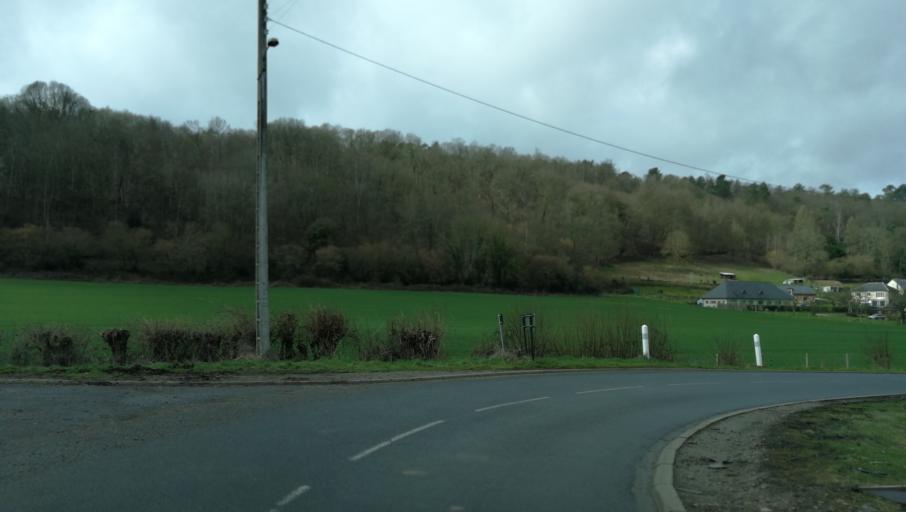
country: FR
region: Haute-Normandie
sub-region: Departement de l'Eure
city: Brionne
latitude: 49.2218
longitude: 0.6976
